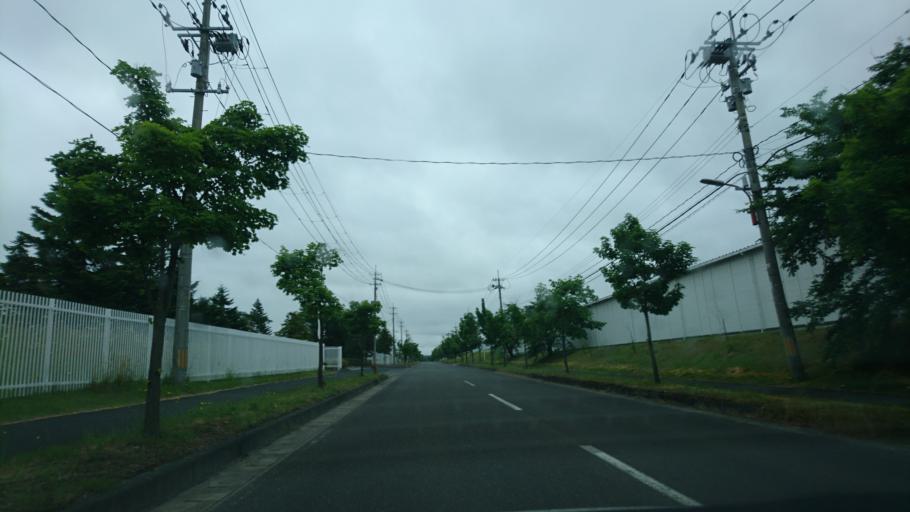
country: JP
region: Iwate
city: Ichinoseki
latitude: 38.9188
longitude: 141.1603
